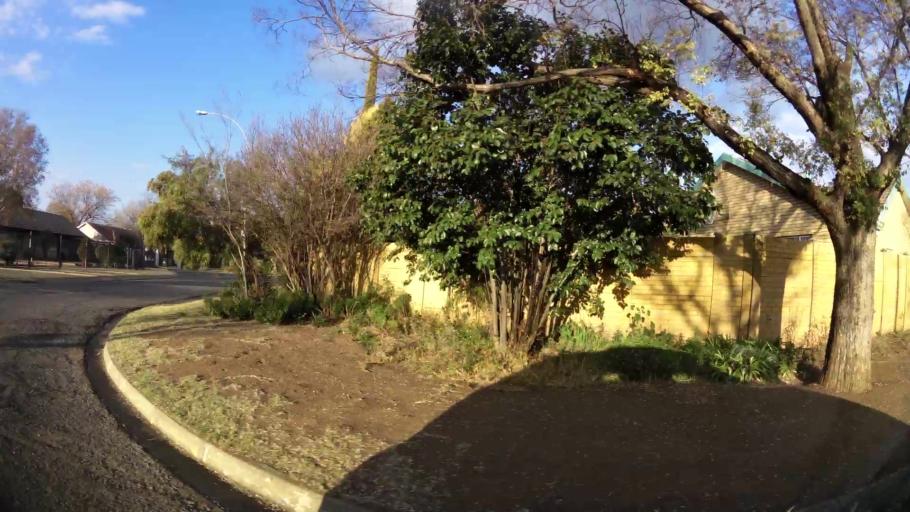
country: ZA
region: Orange Free State
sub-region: Mangaung Metropolitan Municipality
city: Bloemfontein
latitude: -29.1348
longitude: 26.1908
